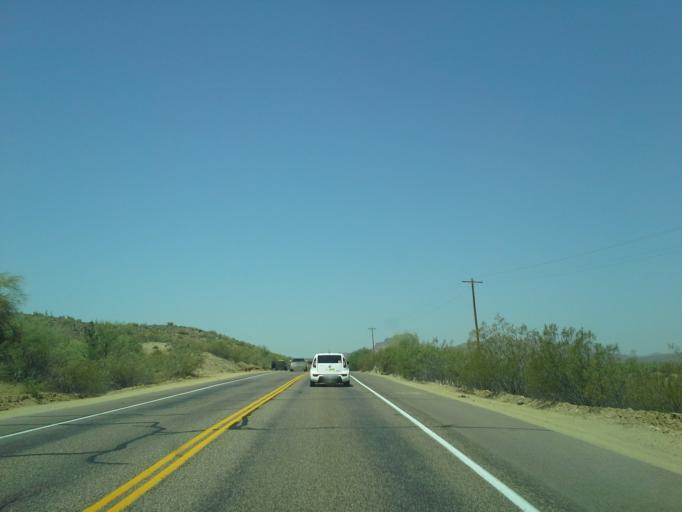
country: US
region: Arizona
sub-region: Maricopa County
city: Fountain Hills
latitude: 33.5471
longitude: -111.5943
